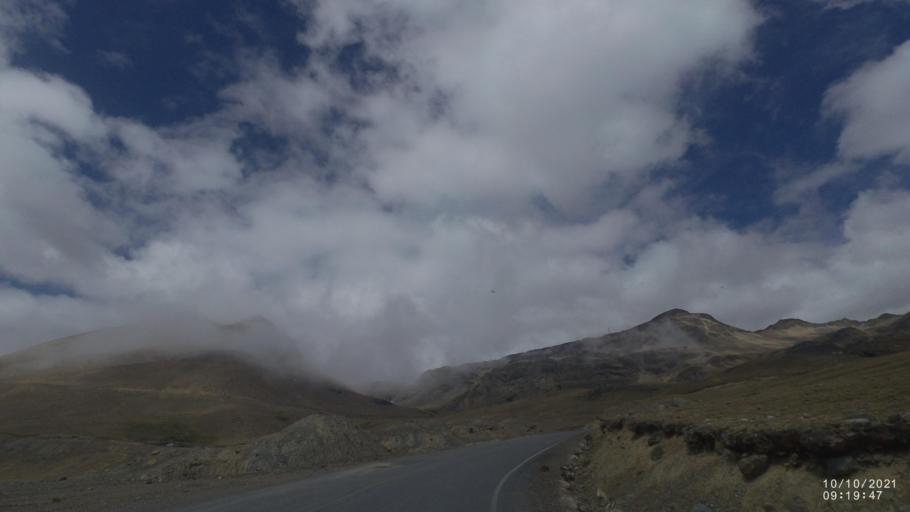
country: BO
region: La Paz
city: Quime
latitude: -17.0563
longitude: -67.3000
